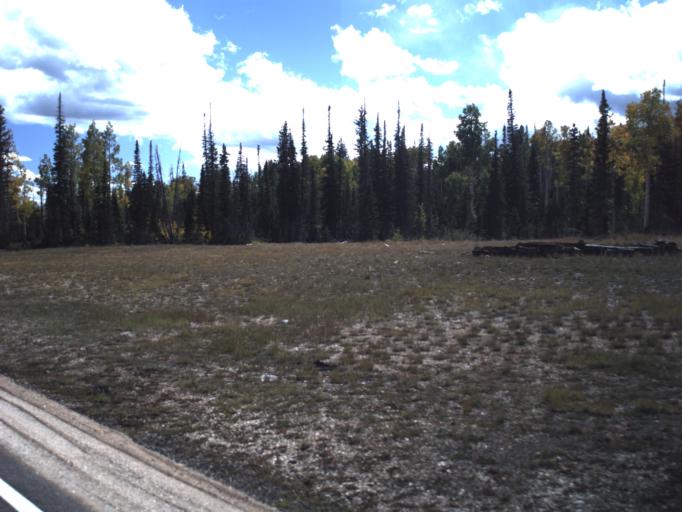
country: US
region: Utah
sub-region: Iron County
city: Parowan
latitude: 37.5519
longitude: -112.7875
